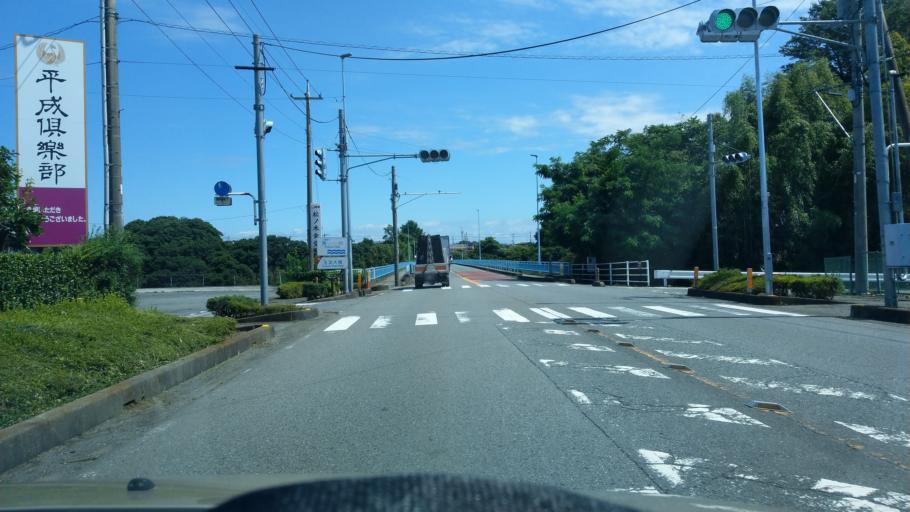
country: JP
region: Saitama
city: Yorii
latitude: 36.1189
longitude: 139.2114
